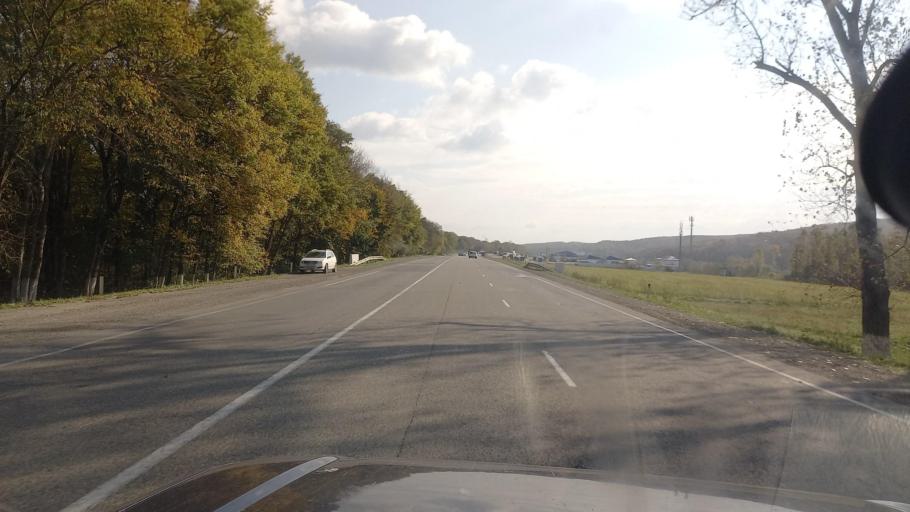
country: RU
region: Krasnodarskiy
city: Gayduk
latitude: 44.8739
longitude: 37.7942
